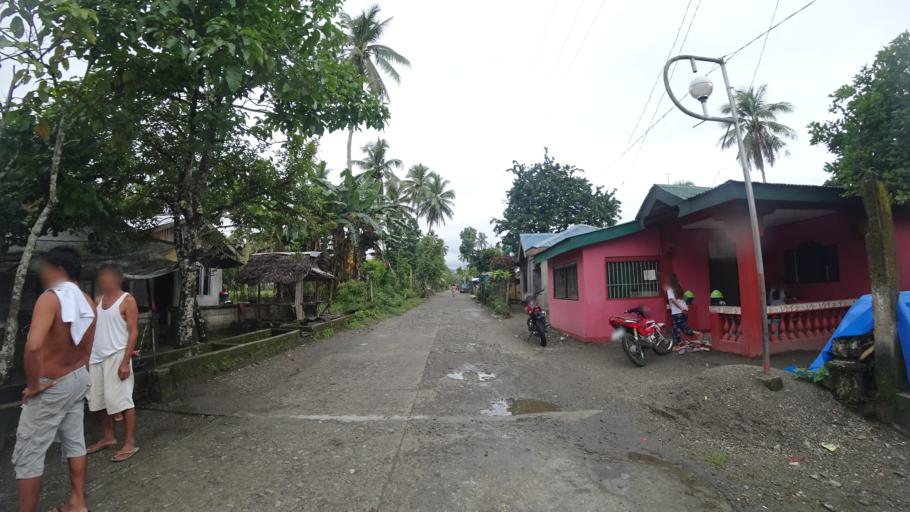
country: PH
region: Eastern Visayas
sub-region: Province of Leyte
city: Bugho
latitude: 10.8231
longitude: 124.9281
